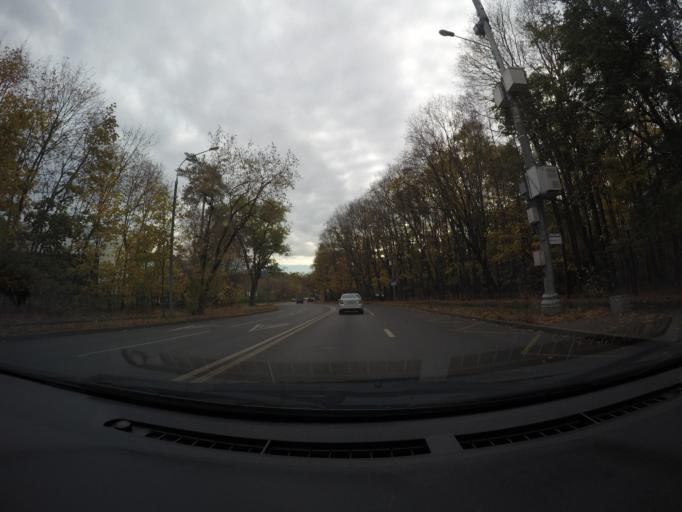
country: RU
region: Moscow
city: Sokol'niki
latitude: 55.8028
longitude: 37.6848
